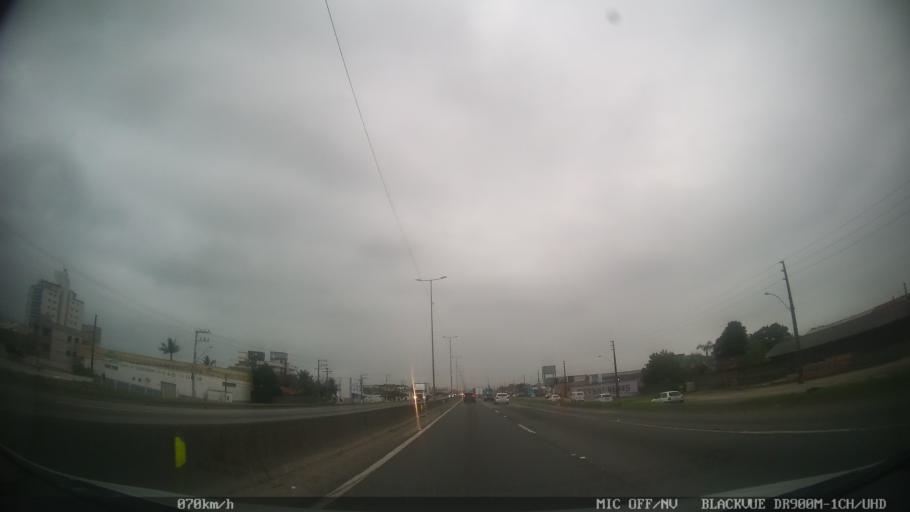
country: BR
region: Santa Catarina
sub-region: Barra Velha
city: Barra Velha
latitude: -26.6526
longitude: -48.6870
